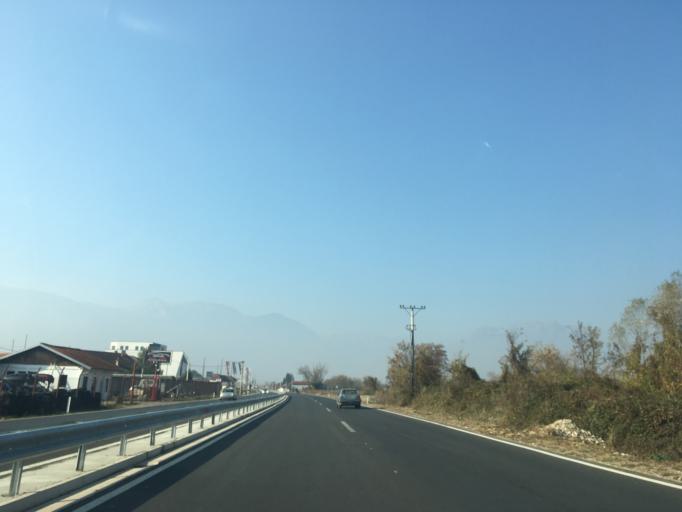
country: XK
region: Pec
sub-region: Komuna e Pejes
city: Dubova (Driloni)
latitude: 42.6595
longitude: 20.3644
